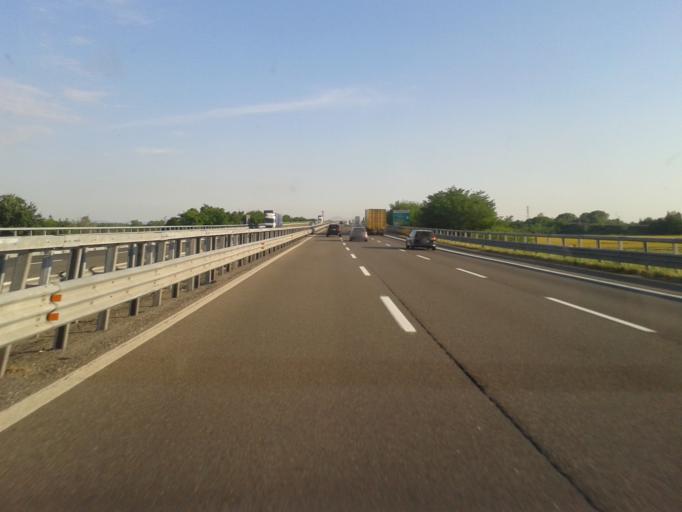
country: IT
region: Piedmont
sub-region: Provincia di Alessandria
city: Tortona
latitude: 44.9025
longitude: 8.8430
